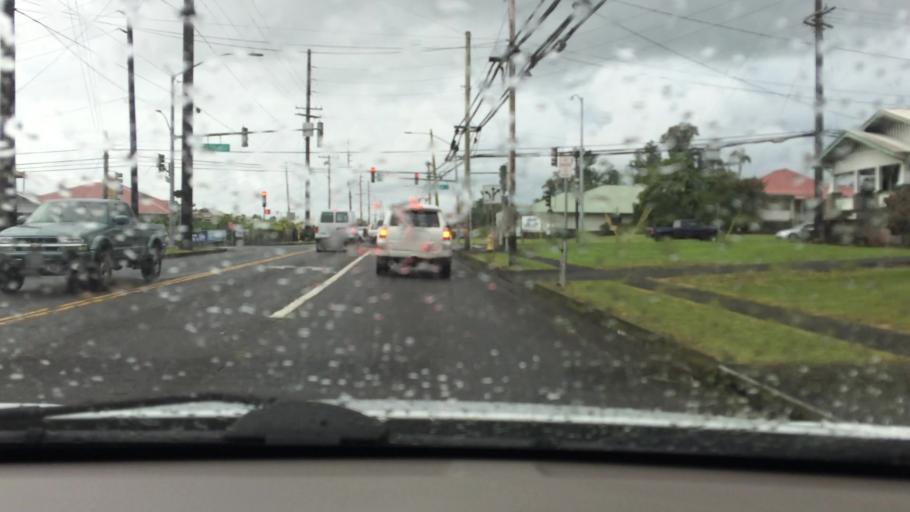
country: US
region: Hawaii
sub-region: Hawaii County
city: Hilo
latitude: 19.7066
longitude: -155.0772
